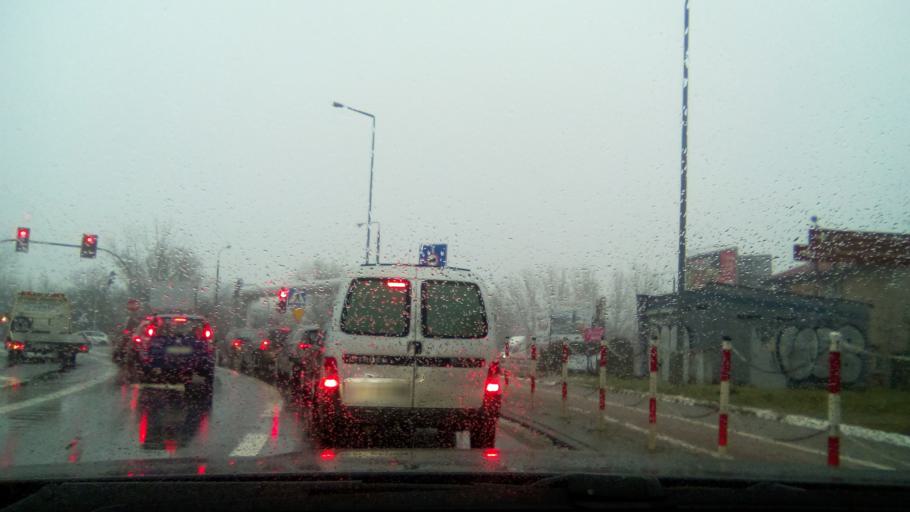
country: PL
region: Greater Poland Voivodeship
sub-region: Powiat poznanski
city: Swarzedz
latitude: 52.4036
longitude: 17.0559
